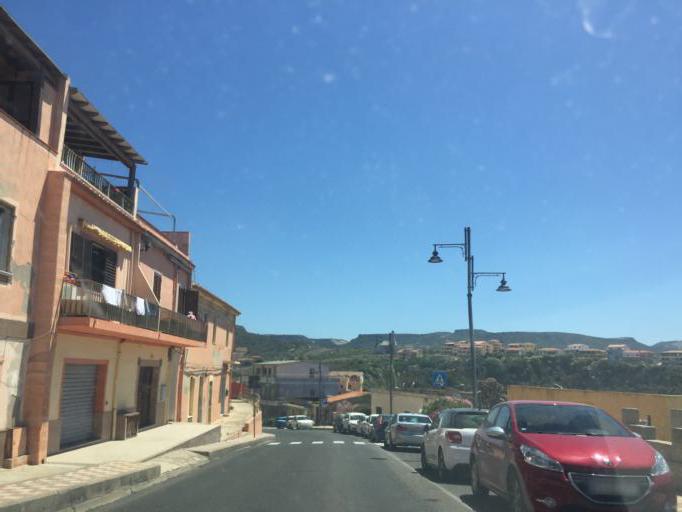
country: IT
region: Sardinia
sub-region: Provincia di Sassari
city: Castelsardo
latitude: 40.9156
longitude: 8.7111
